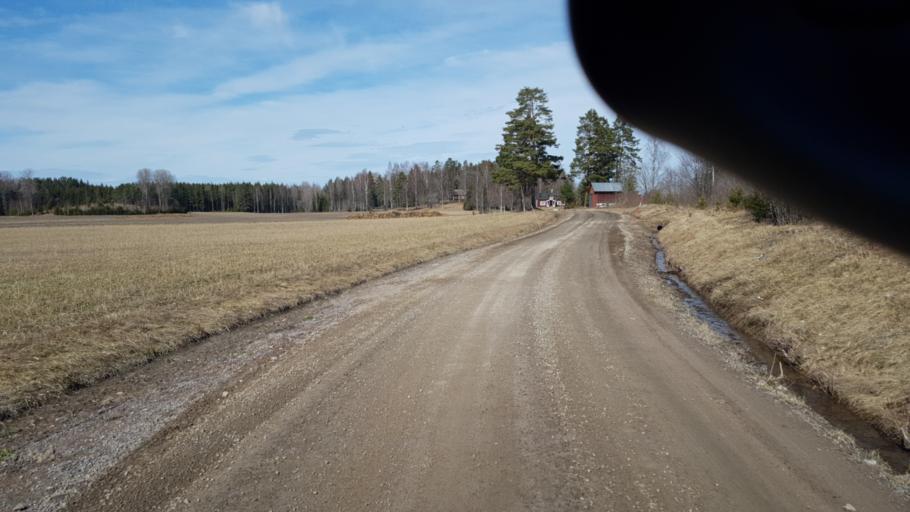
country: SE
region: Vaermland
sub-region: Grums Kommun
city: Grums
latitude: 59.5258
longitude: 12.9195
